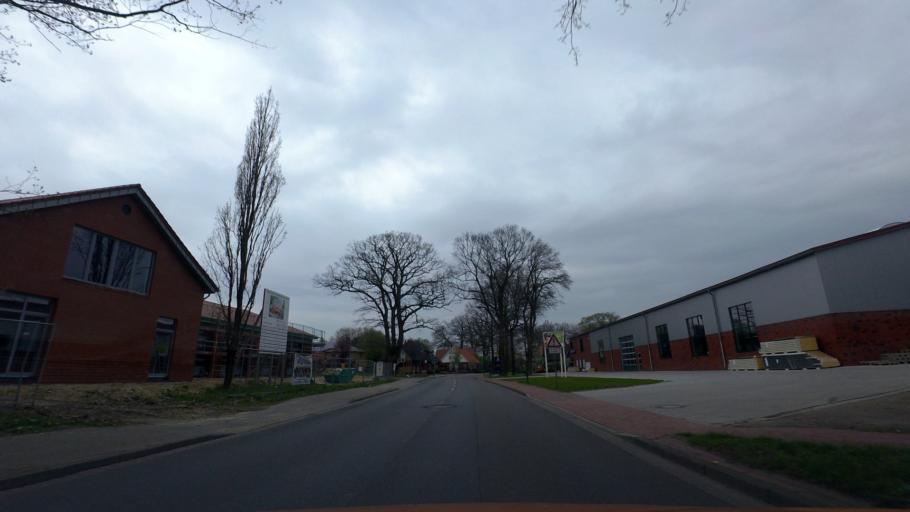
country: DE
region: Lower Saxony
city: Essen
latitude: 52.7242
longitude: 8.0072
